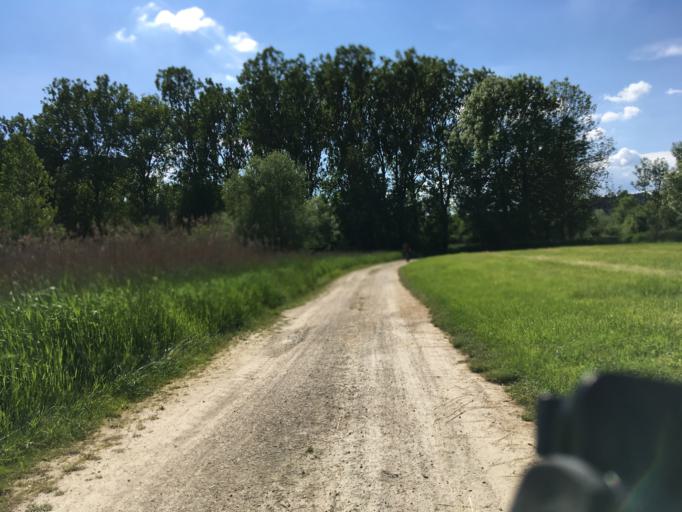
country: CH
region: Schaffhausen
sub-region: Bezirk Reiat
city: Thayngen
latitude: 47.7960
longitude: 8.7071
